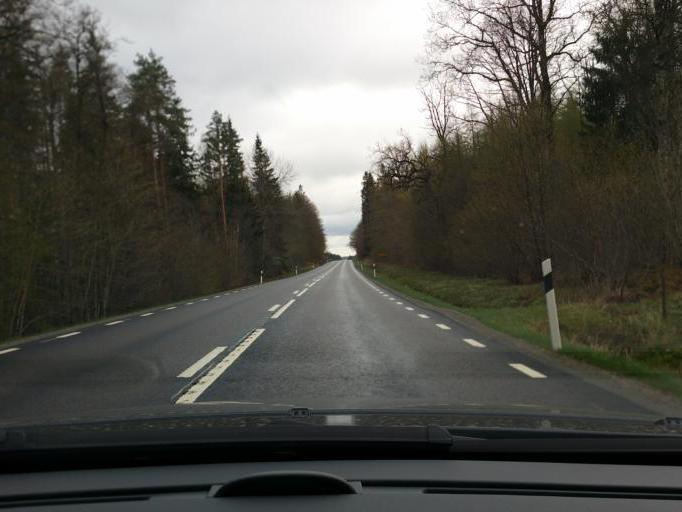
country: SE
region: Kronoberg
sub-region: Alvesta Kommun
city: Moheda
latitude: 57.0291
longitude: 14.6565
